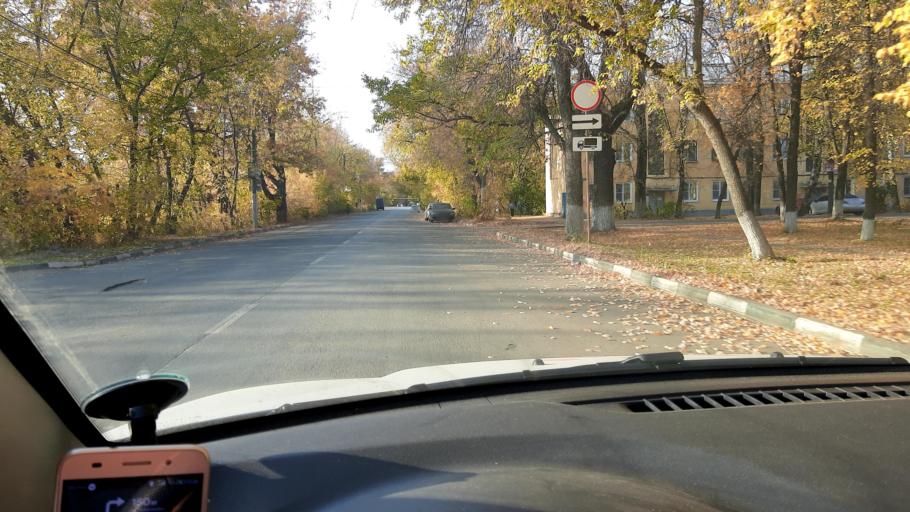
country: RU
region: Nizjnij Novgorod
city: Nizhniy Novgorod
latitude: 56.2662
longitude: 43.9290
